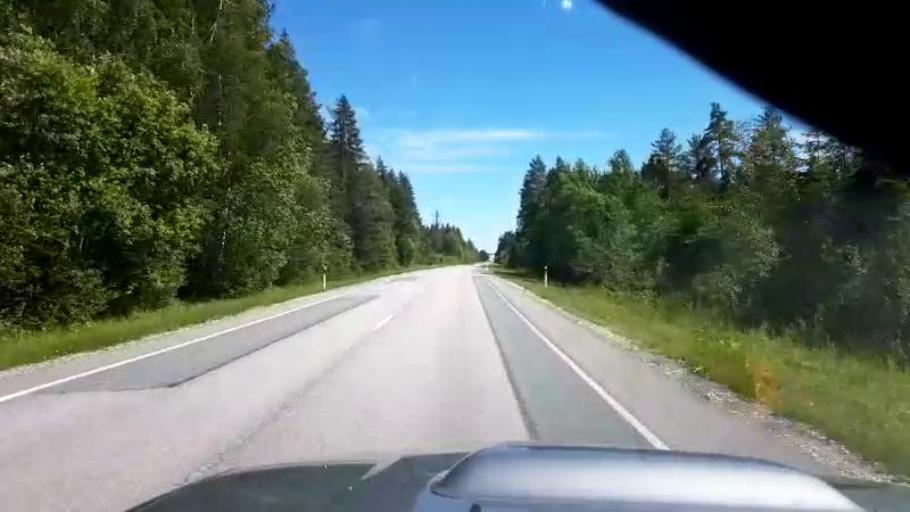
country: EE
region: Jaervamaa
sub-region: Koeru vald
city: Koeru
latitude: 58.9725
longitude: 26.1265
